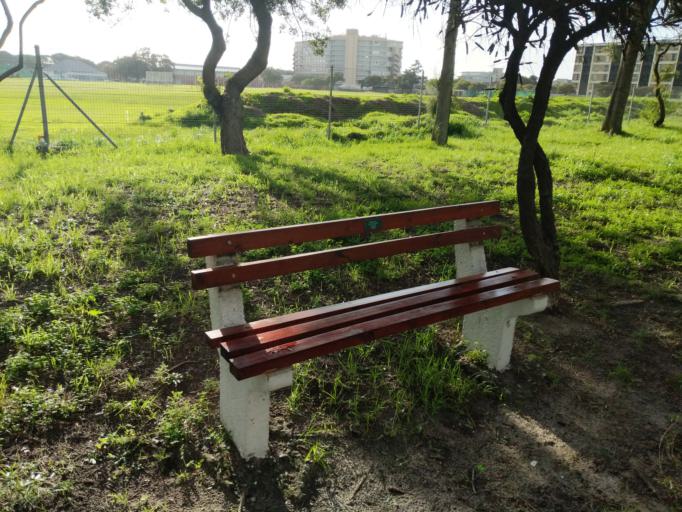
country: ZA
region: Western Cape
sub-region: City of Cape Town
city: Rosebank
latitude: -33.9388
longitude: 18.5098
